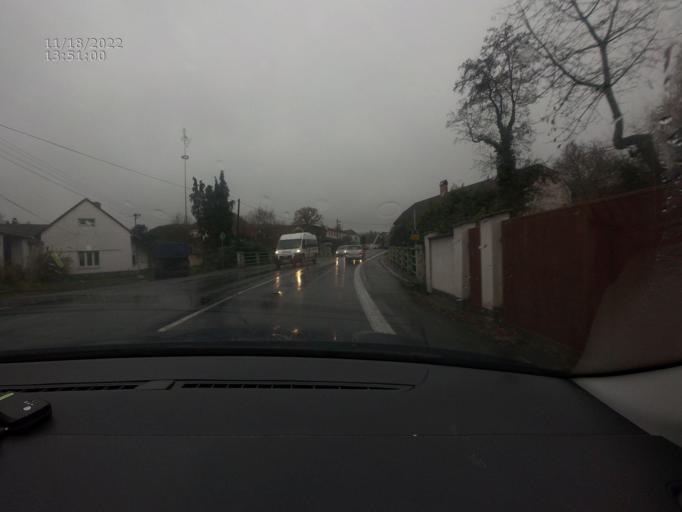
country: CZ
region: Jihocesky
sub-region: Okres Strakonice
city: Blatna
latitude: 49.4014
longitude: 13.9057
